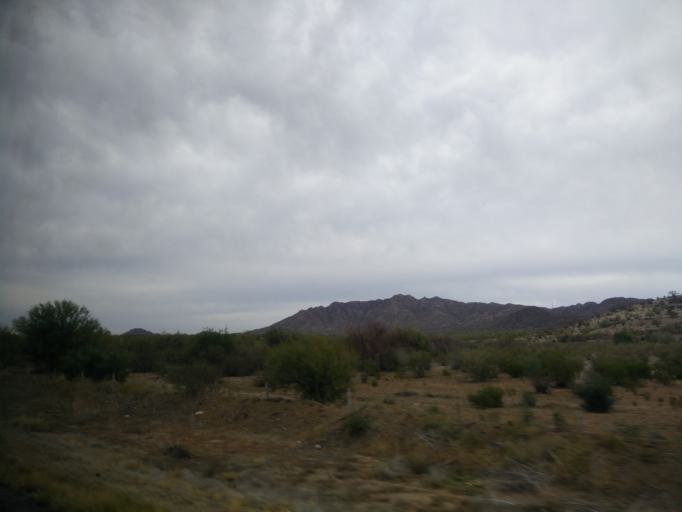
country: MX
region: Sonora
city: Hermosillo
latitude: 28.9410
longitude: -110.9597
